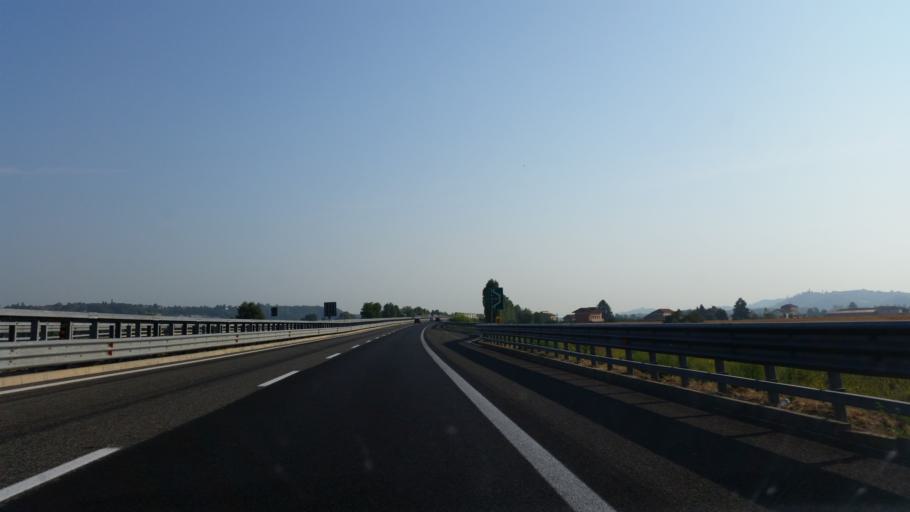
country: IT
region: Piedmont
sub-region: Provincia di Asti
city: San Martino Alfieri
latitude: 44.8118
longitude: 8.1365
